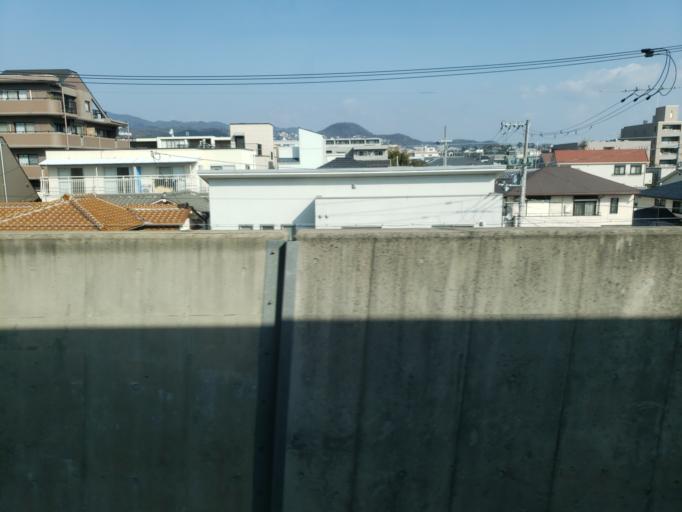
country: JP
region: Hyogo
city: Nishinomiya-hama
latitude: 34.7392
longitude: 135.3298
